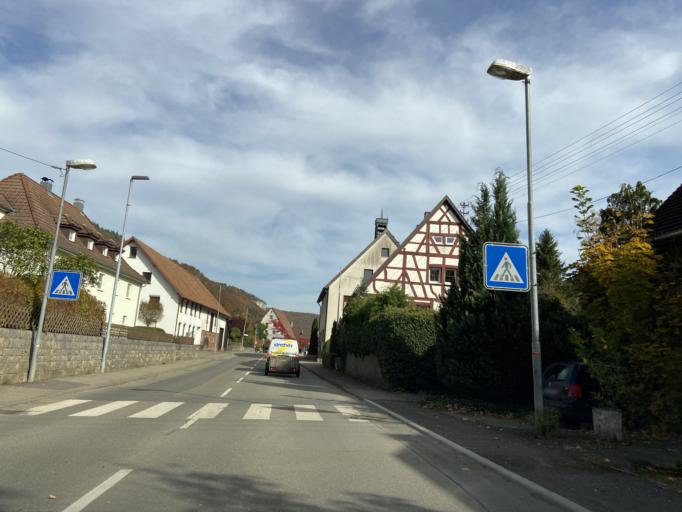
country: DE
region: Baden-Wuerttemberg
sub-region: Tuebingen Region
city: Schwenningen
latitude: 48.0838
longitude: 9.0378
